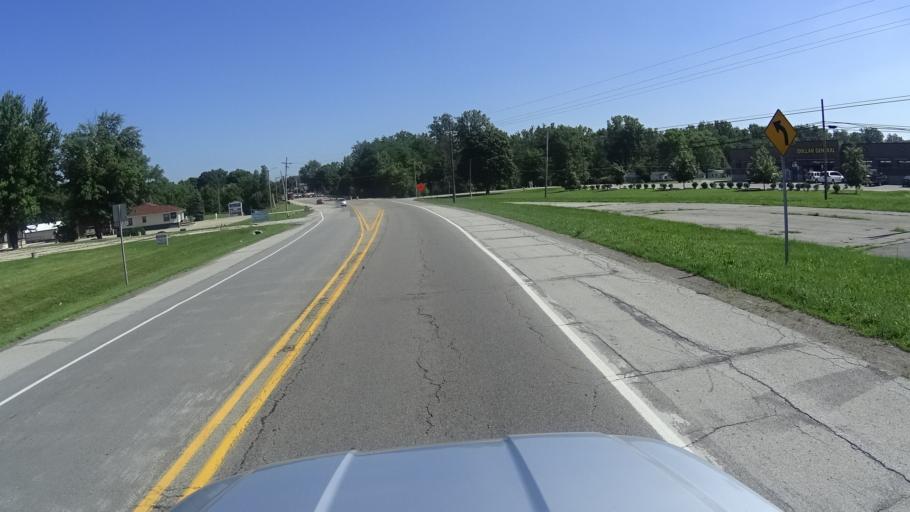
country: US
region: Indiana
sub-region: Madison County
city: Pendleton
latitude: 40.0045
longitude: -85.7304
